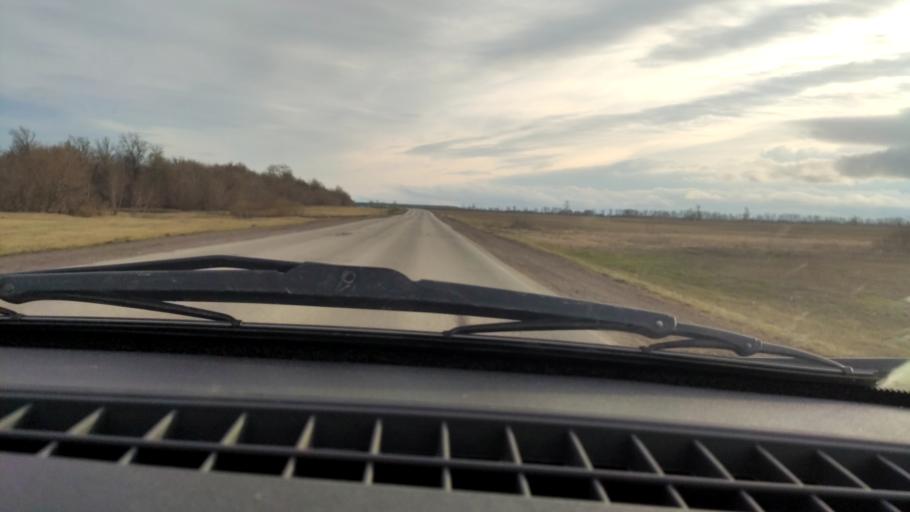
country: RU
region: Bashkortostan
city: Davlekanovo
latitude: 54.2811
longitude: 55.1093
